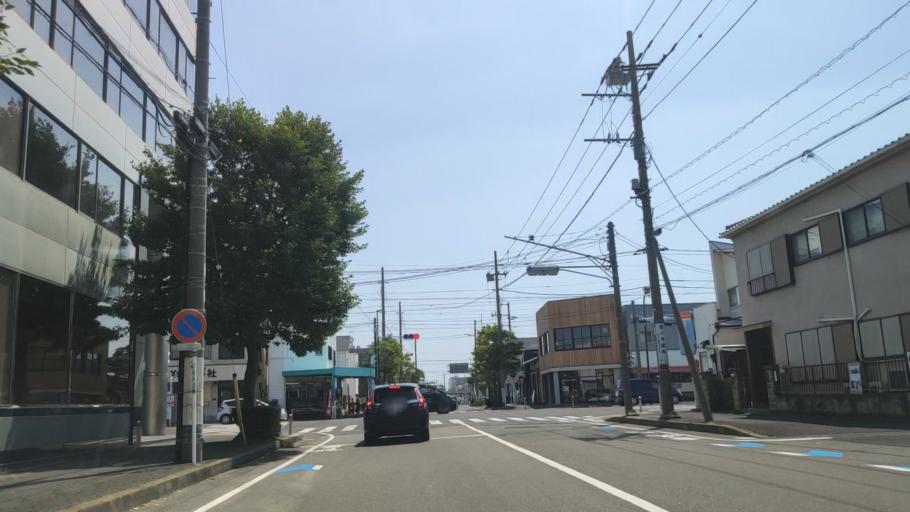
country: JP
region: Kanagawa
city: Hiratsuka
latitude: 35.3278
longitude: 139.3371
